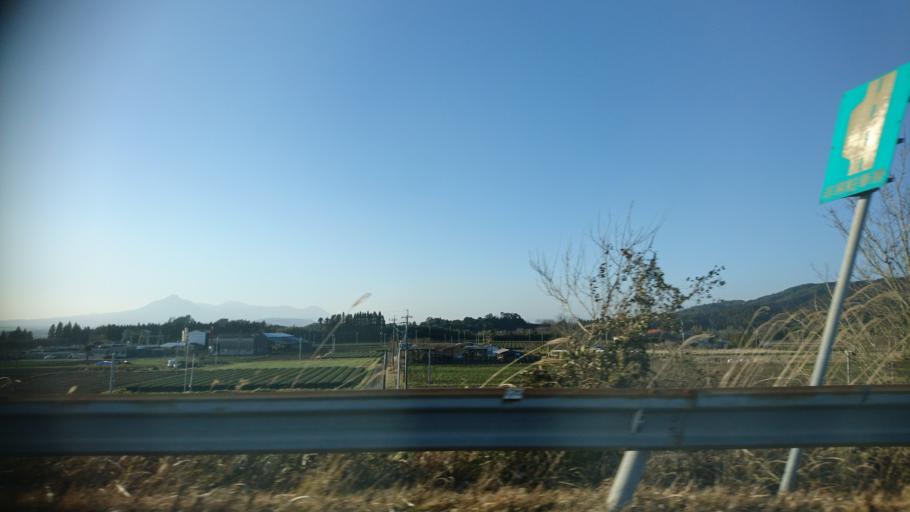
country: JP
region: Miyazaki
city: Miyakonojo
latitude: 31.7917
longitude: 131.1552
